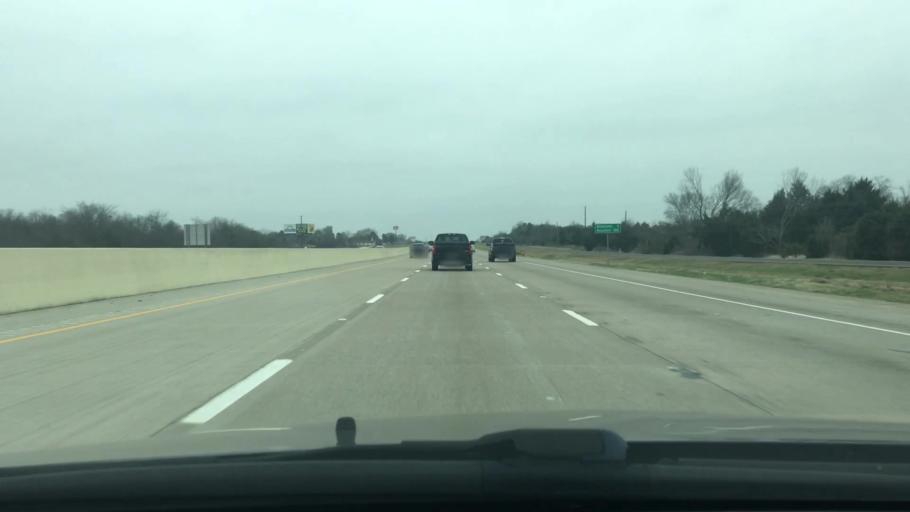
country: US
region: Texas
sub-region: Navarro County
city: Corsicana
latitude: 31.9994
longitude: -96.4302
